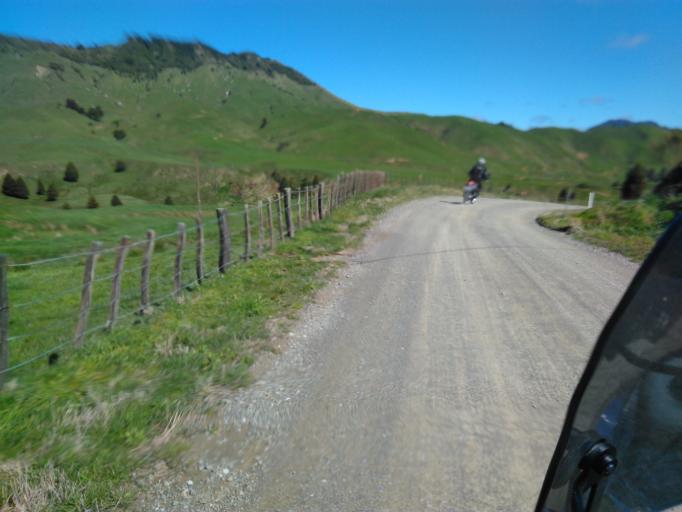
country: NZ
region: Bay of Plenty
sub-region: Opotiki District
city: Opotiki
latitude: -38.3023
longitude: 177.5608
